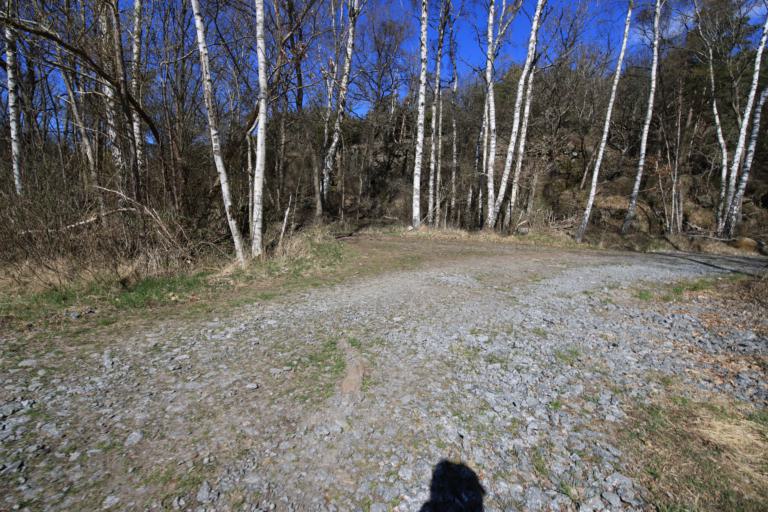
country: SE
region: Halland
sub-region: Varbergs Kommun
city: Varberg
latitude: 57.1870
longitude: 12.2294
